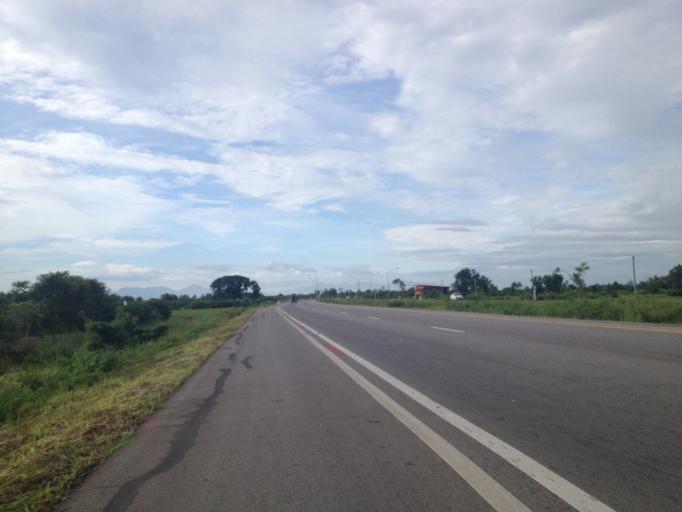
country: TH
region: Chiang Mai
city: San Pa Tong
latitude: 18.5552
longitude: 98.8497
